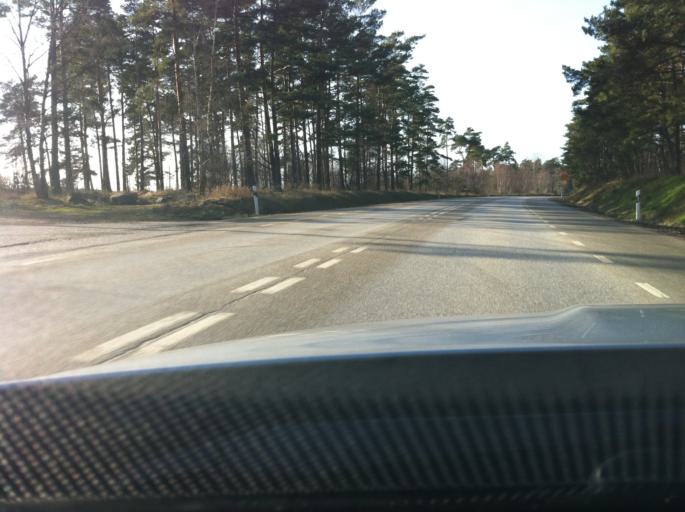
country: SE
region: Skane
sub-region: Kavlinge Kommun
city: Hofterup
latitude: 55.8250
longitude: 12.9482
